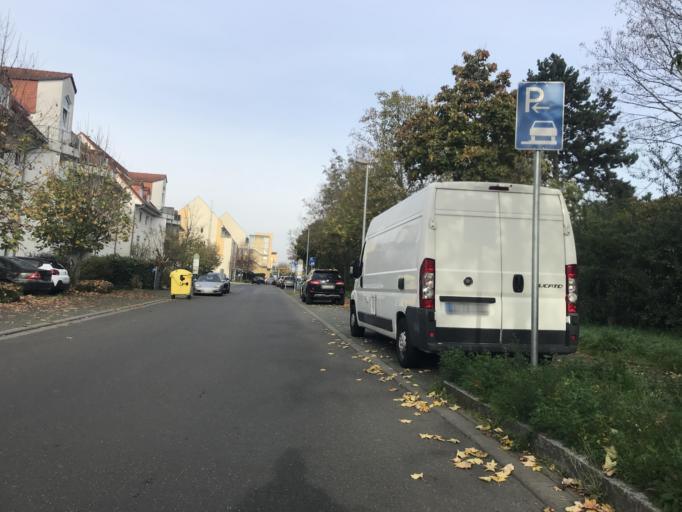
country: DE
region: Rheinland-Pfalz
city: Mainz
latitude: 50.0167
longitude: 8.3026
